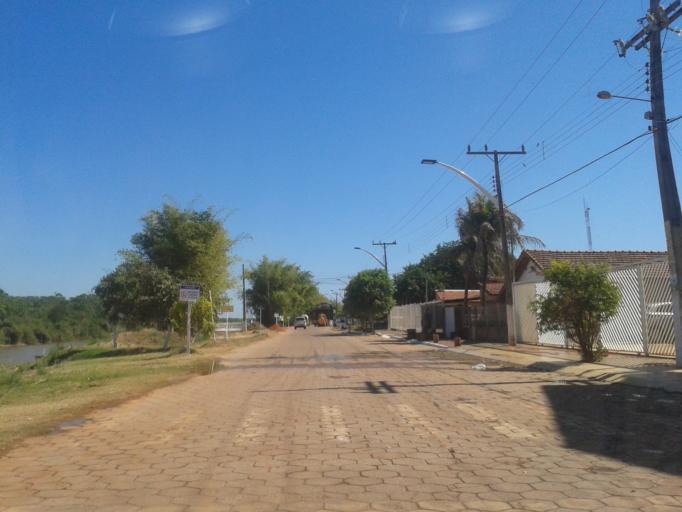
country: BR
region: Goias
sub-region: Sao Miguel Do Araguaia
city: Sao Miguel do Araguaia
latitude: -13.2187
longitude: -50.5758
